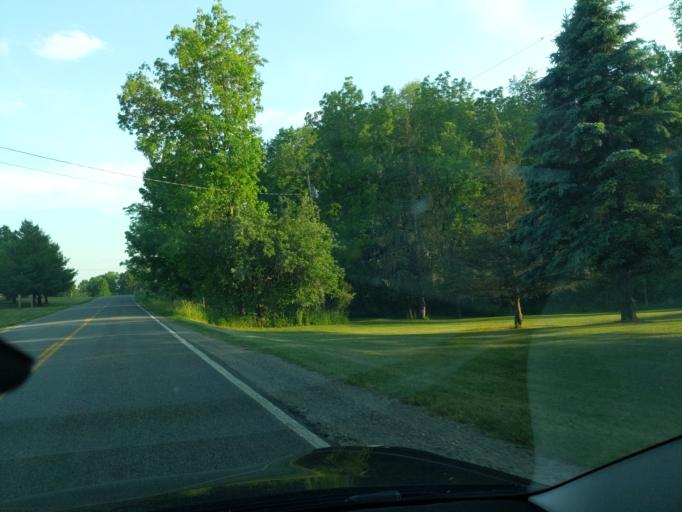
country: US
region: Michigan
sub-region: Barry County
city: Nashville
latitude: 42.5542
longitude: -85.0940
